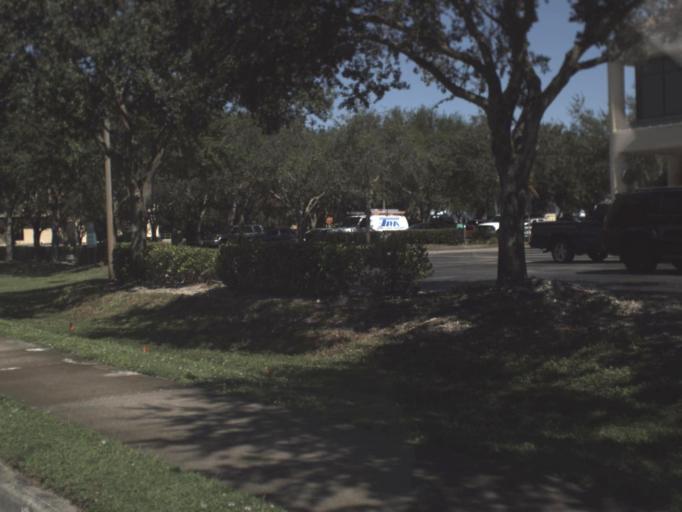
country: US
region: Florida
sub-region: Collier County
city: Naples
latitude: 26.1536
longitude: -81.7667
